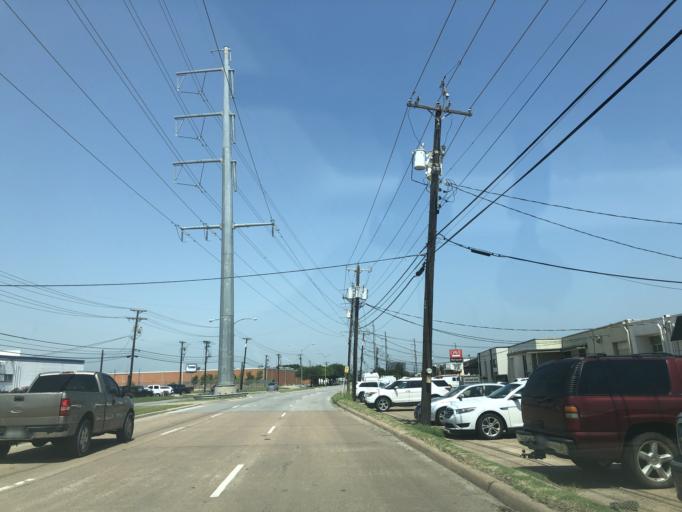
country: US
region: Texas
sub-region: Dallas County
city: Dallas
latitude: 32.7967
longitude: -96.8362
